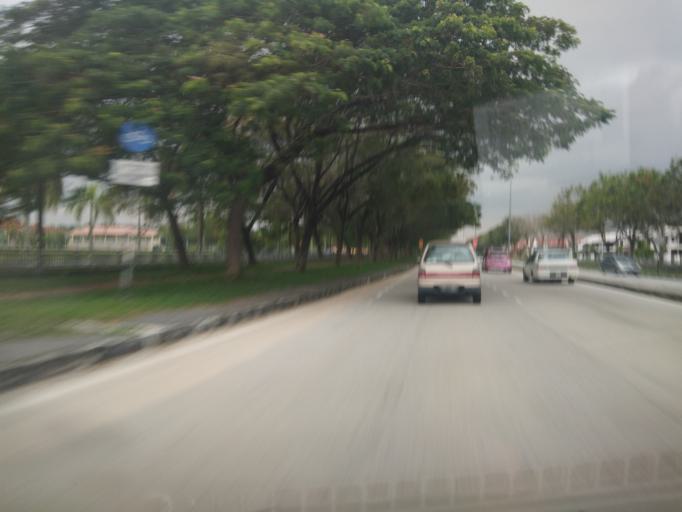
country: MY
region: Penang
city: Kepala Batas
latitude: 5.5195
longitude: 100.4714
